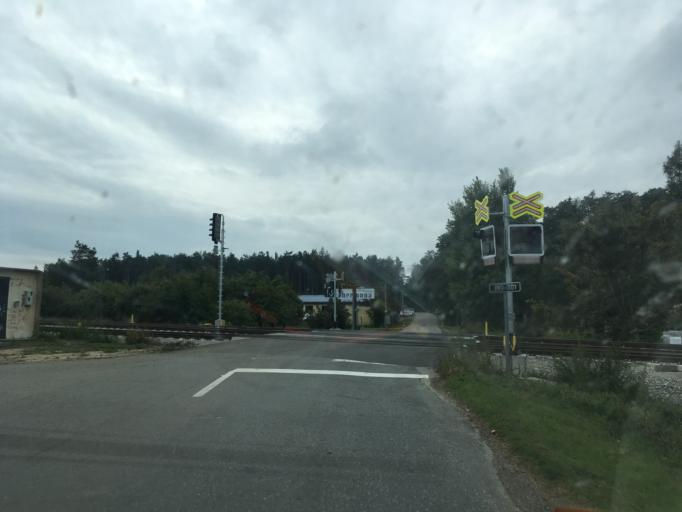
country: CZ
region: South Moravian
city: Zbraslav
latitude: 49.1849
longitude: 16.2550
